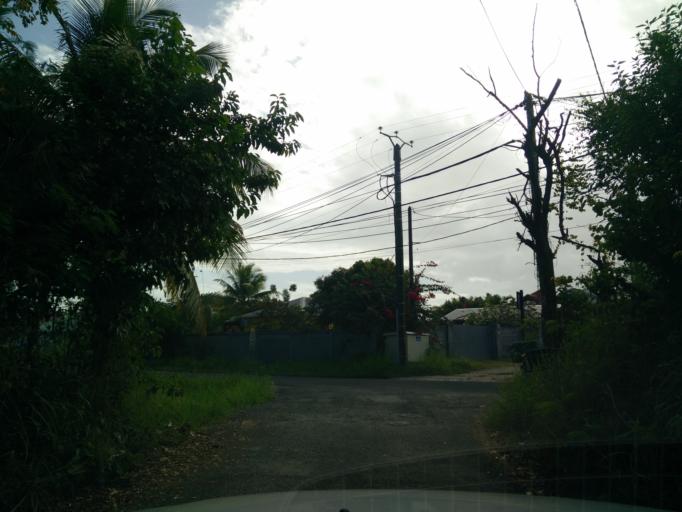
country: GP
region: Guadeloupe
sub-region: Guadeloupe
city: Sainte-Anne
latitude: 16.2468
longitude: -61.3804
